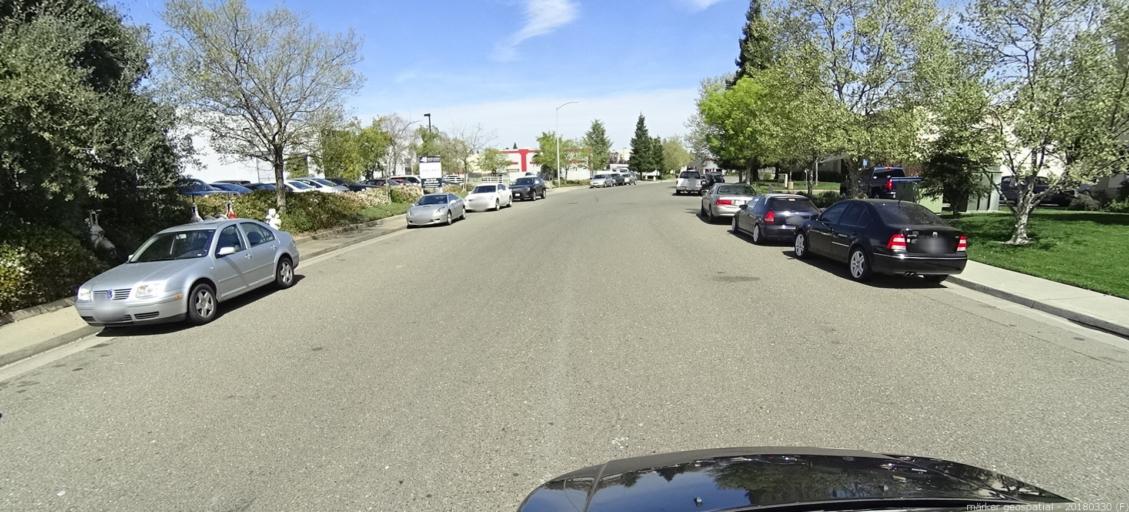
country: US
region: California
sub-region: Sacramento County
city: Rosemont
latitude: 38.5371
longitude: -121.3571
